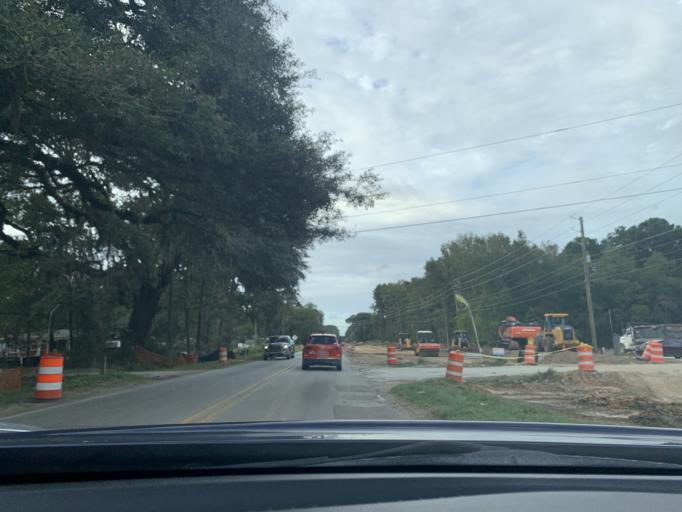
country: US
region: Georgia
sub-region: Chatham County
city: Georgetown
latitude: 32.0148
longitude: -81.2339
